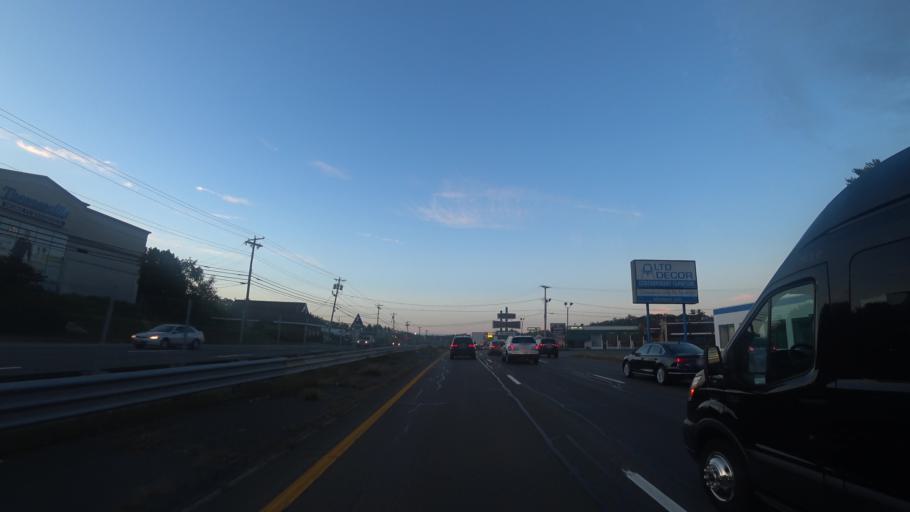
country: US
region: Massachusetts
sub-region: Essex County
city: Saugus
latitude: 42.4764
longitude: -71.0235
